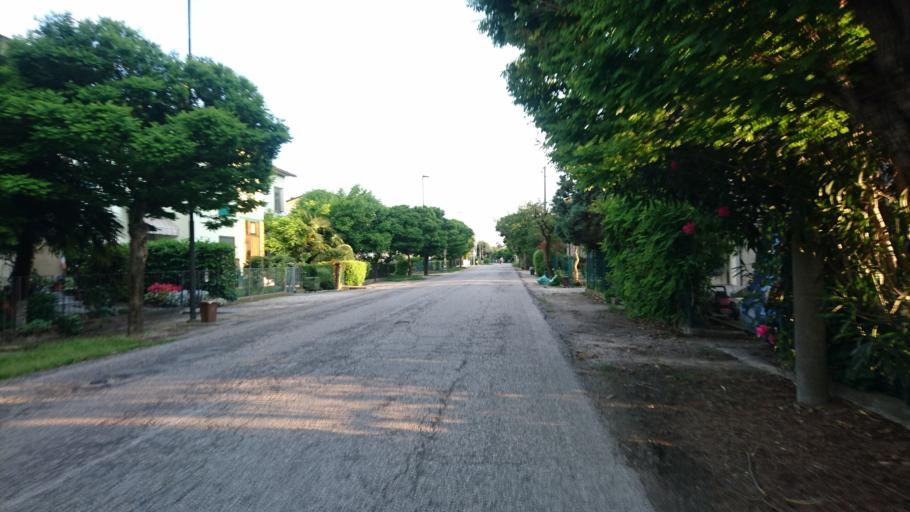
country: IT
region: Veneto
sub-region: Provincia di Rovigo
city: Castelmassa
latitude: 45.0201
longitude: 11.3160
